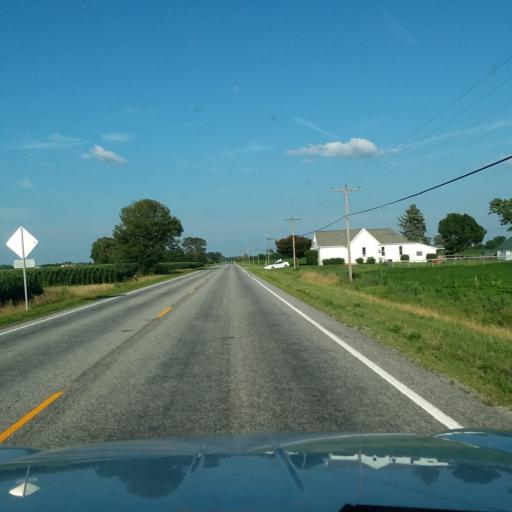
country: US
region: Indiana
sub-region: Johnson County
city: Princes Lakes
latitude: 39.4103
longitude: -86.0775
